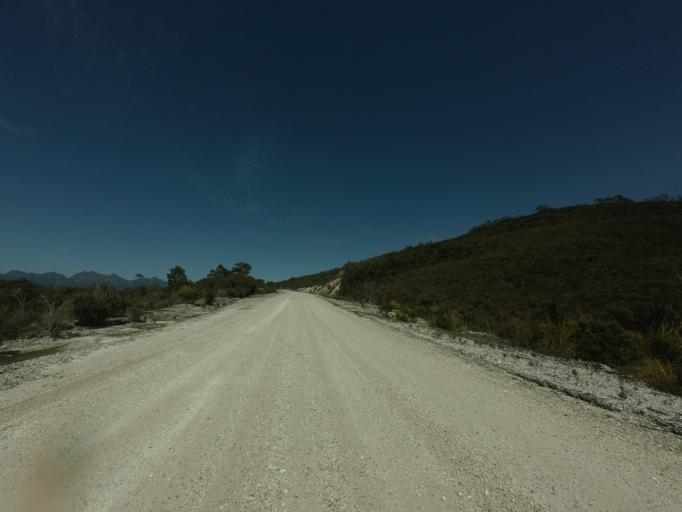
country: AU
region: Tasmania
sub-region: Huon Valley
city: Geeveston
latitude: -43.0339
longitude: 146.2926
